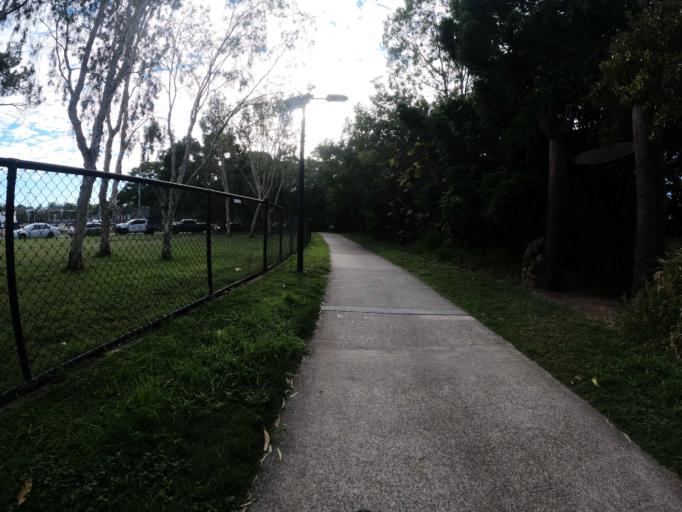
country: AU
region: Queensland
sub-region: Brisbane
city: Windsor
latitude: -27.4437
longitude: 153.0265
